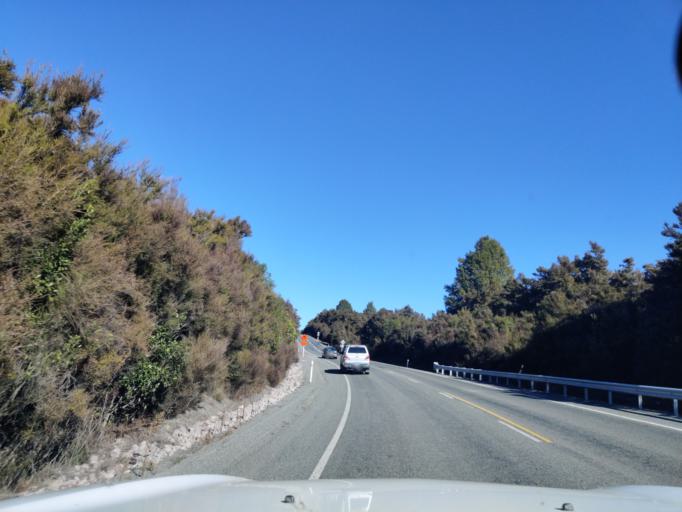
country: NZ
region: Waikato
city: Turangi
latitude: -39.1427
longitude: 175.7720
